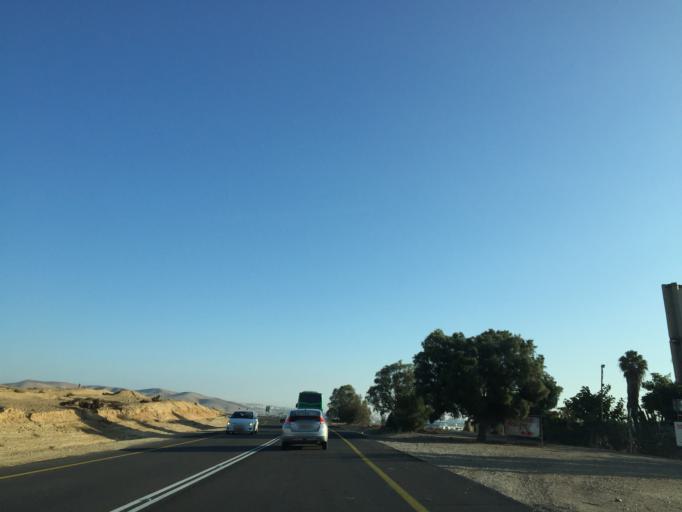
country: IL
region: Southern District
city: Dimona
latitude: 31.0528
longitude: 34.9961
